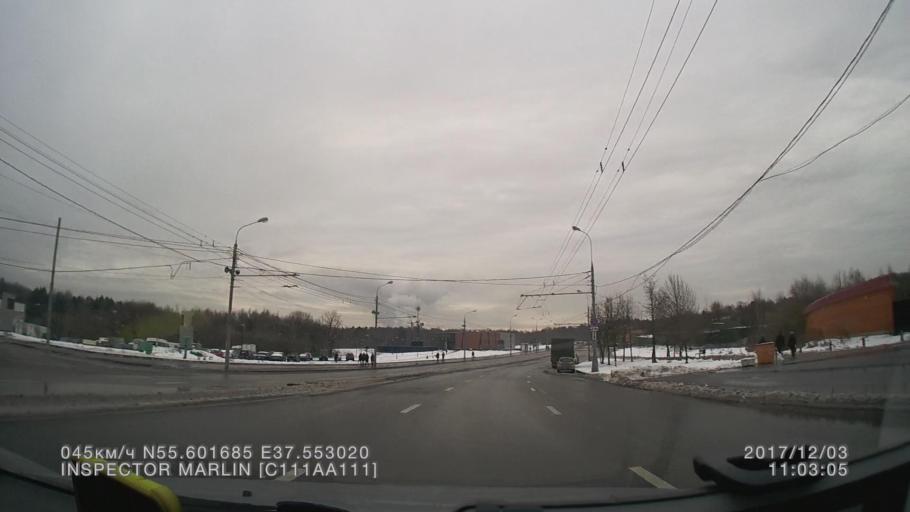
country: RU
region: Moscow
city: Yasenevo
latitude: 55.6017
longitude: 37.5531
